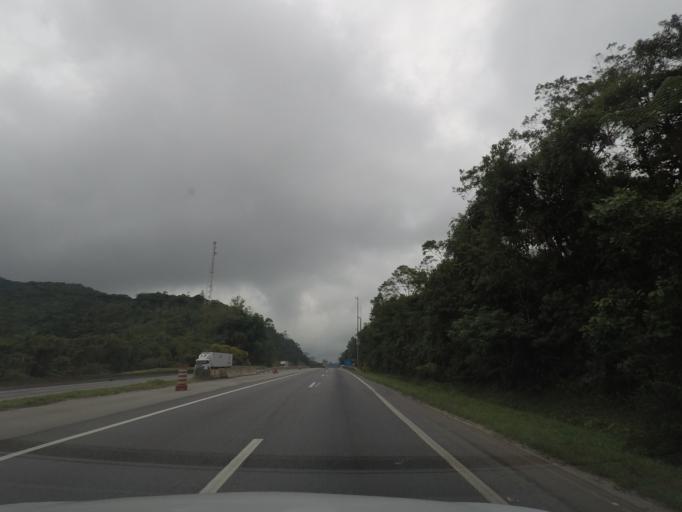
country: BR
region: Sao Paulo
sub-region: Juquitiba
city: Juquitiba
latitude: -24.0290
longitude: -47.1766
